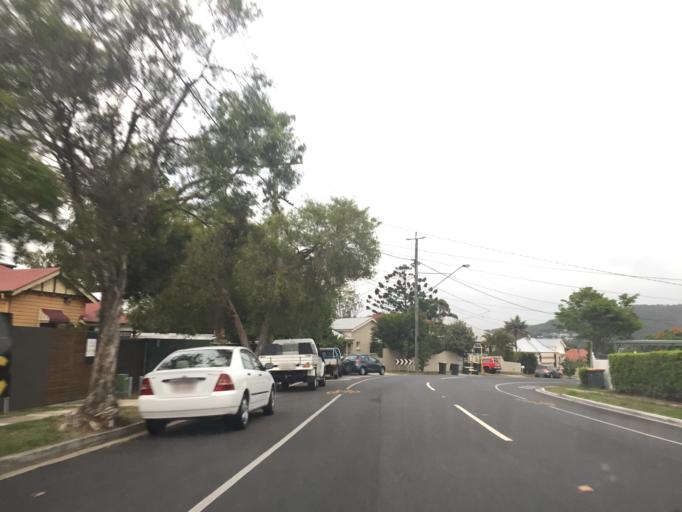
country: AU
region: Queensland
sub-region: Brisbane
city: Milton
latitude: -27.4559
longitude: 152.9829
